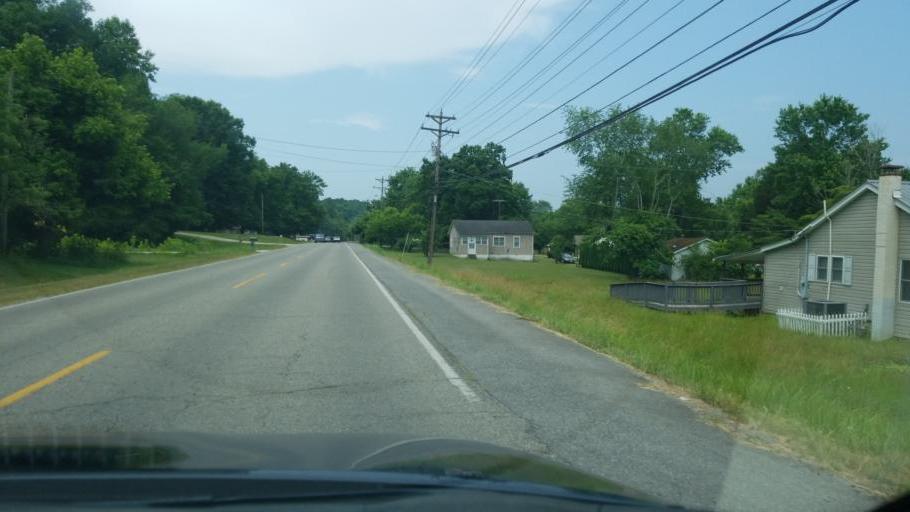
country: US
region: Tennessee
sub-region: Humphreys County
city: Waverly
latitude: 36.0806
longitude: -87.8255
